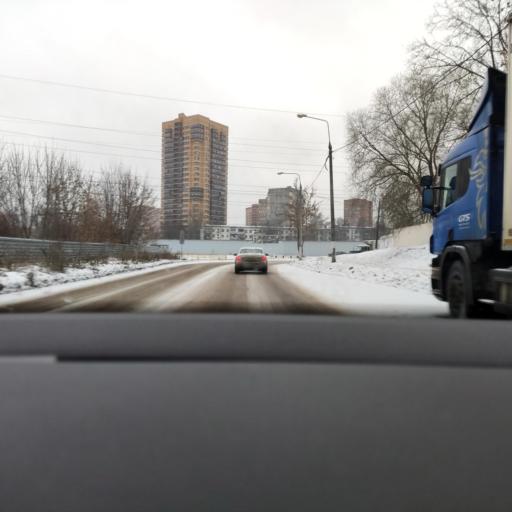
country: RU
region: Moskovskaya
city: Reutov
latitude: 55.7710
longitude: 37.8556
